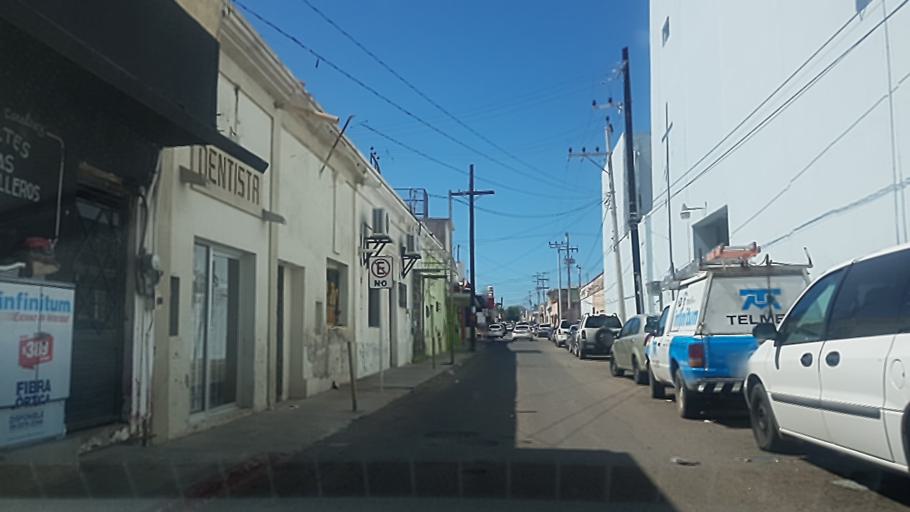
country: MX
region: Sonora
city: Heroica Guaymas
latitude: 27.9242
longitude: -110.8930
